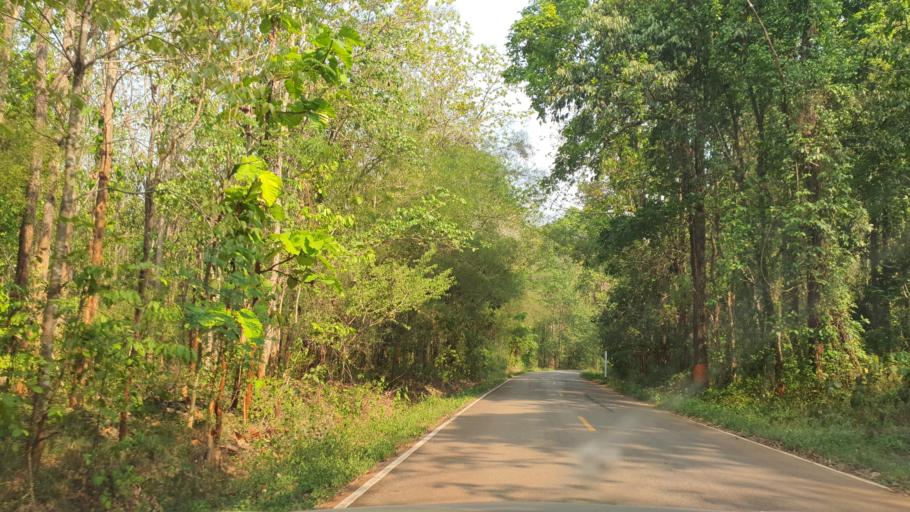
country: TH
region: Chiang Mai
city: San Sai
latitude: 19.0059
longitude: 99.1242
